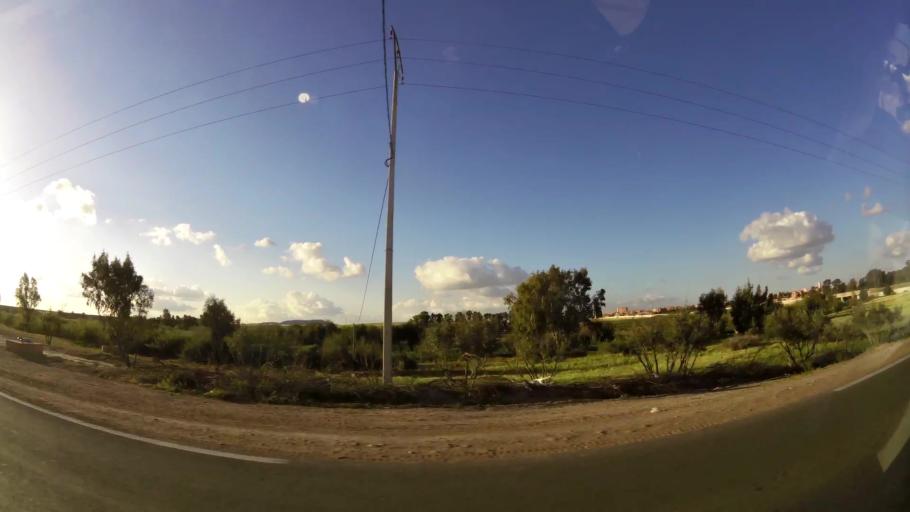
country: MA
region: Marrakech-Tensift-Al Haouz
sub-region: Kelaa-Des-Sraghna
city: Sidi Bou Othmane
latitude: 32.2281
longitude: -7.9673
